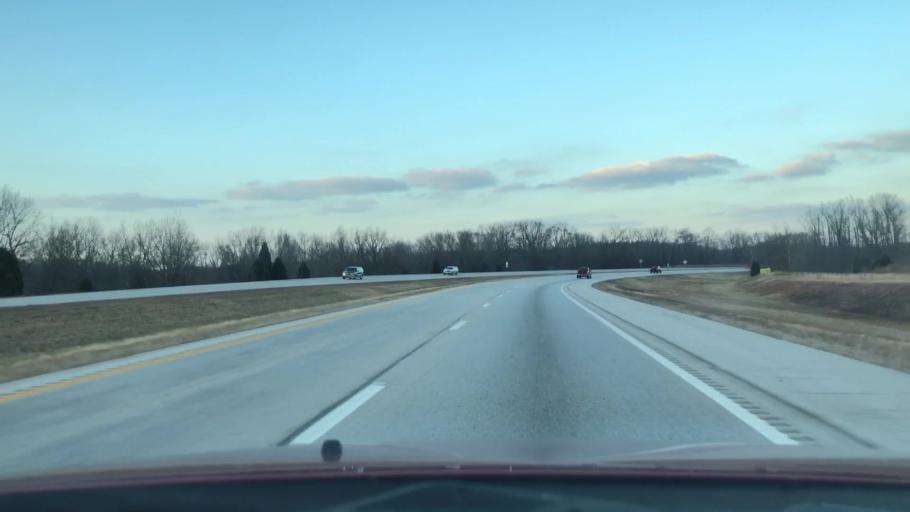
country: US
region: Missouri
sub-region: Christian County
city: Ozark
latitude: 36.9194
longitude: -93.2430
